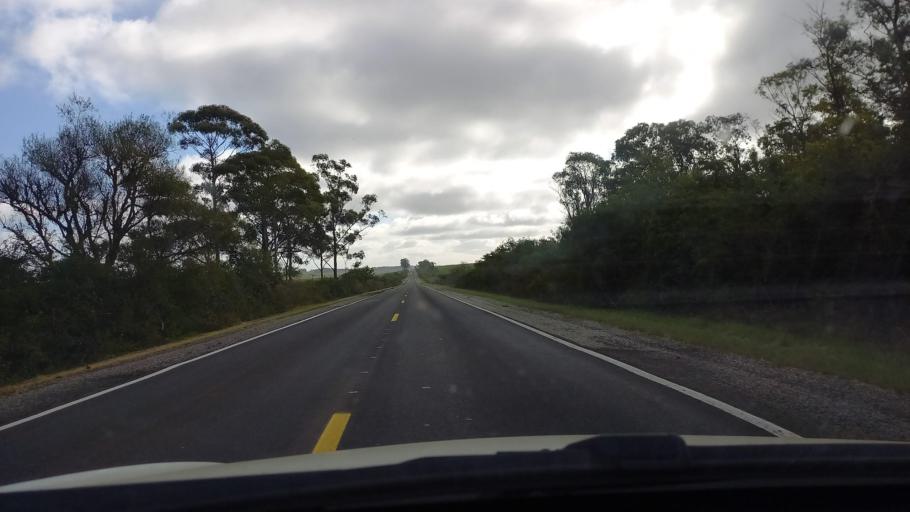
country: BR
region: Rio Grande do Sul
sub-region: Dom Pedrito
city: Dom Pedrito
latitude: -30.8981
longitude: -54.8422
